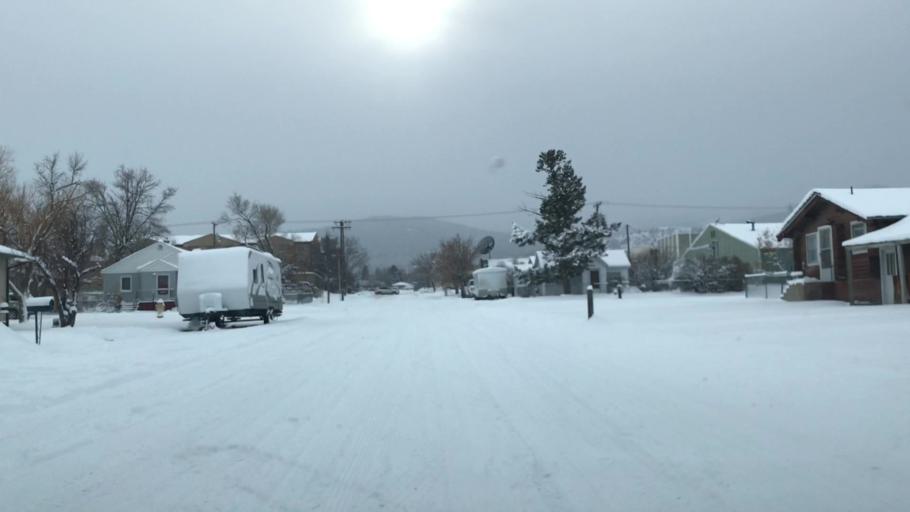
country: US
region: Montana
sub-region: Lewis and Clark County
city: Helena
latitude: 46.5927
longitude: -112.0111
